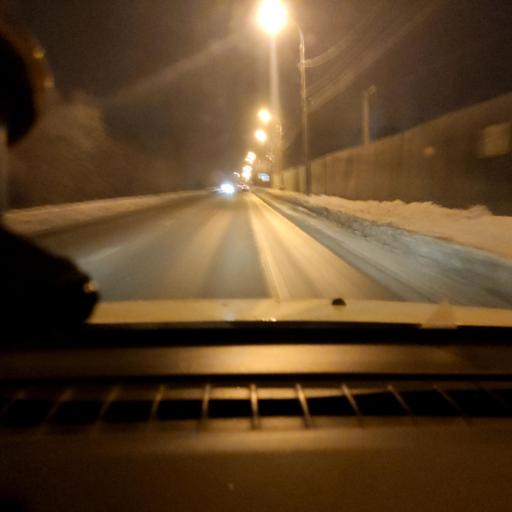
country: RU
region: Samara
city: Rozhdestveno
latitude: 53.1558
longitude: 50.0710
